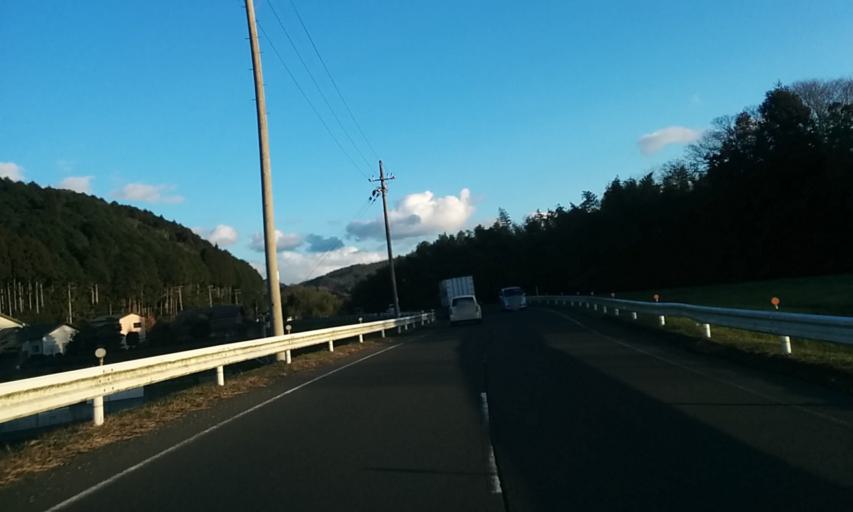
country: JP
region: Kyoto
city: Ayabe
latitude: 35.3111
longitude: 135.2606
